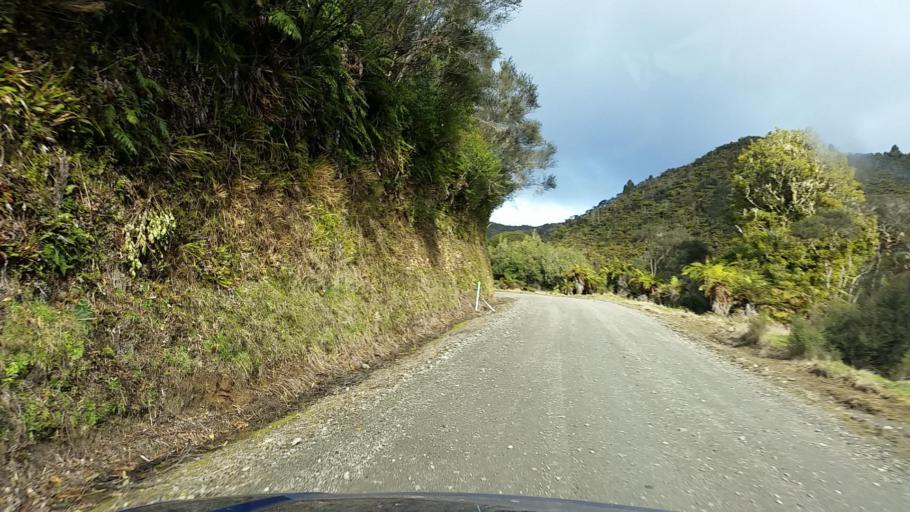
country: NZ
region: Taranaki
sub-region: South Taranaki District
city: Eltham
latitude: -39.2717
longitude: 174.7440
